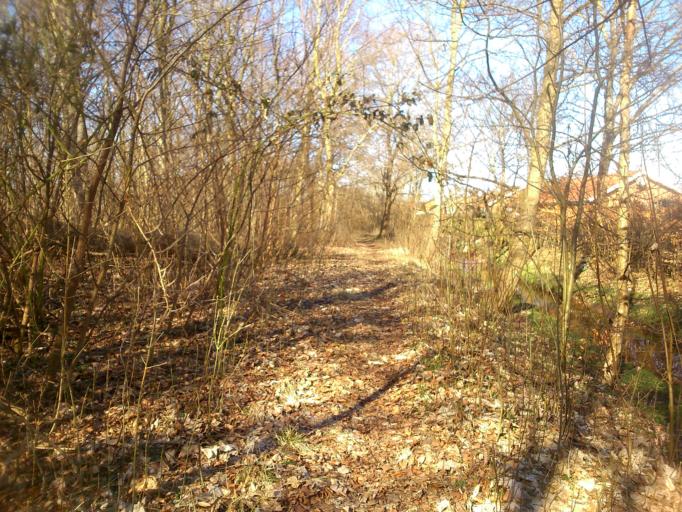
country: DK
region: Central Jutland
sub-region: Ringkobing-Skjern Kommune
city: Ringkobing
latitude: 56.0904
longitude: 8.2546
